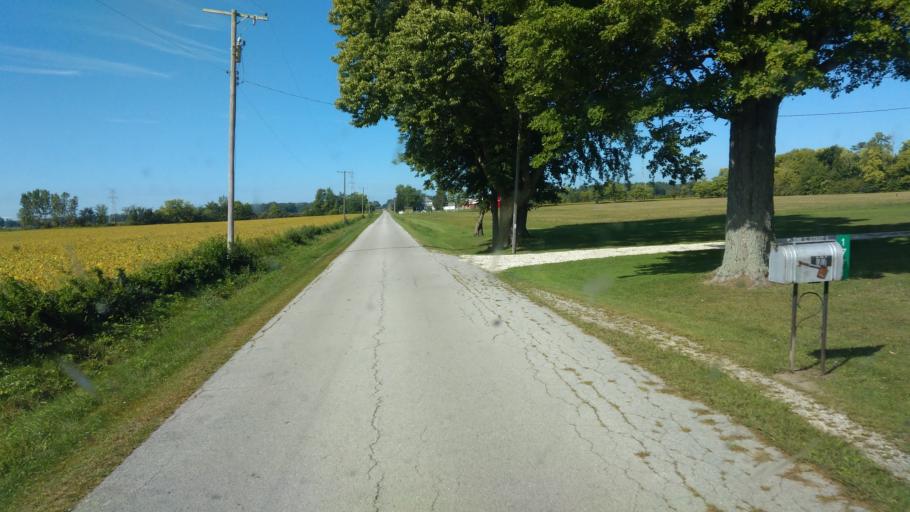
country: US
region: Ohio
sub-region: Sandusky County
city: Clyde
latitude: 41.3914
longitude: -82.9636
